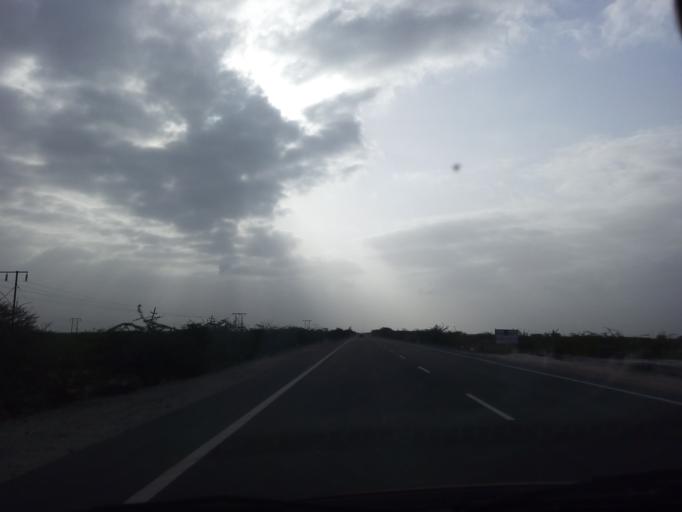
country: IN
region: Gujarat
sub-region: Kachchh
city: Anjar
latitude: 23.2657
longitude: 69.9513
